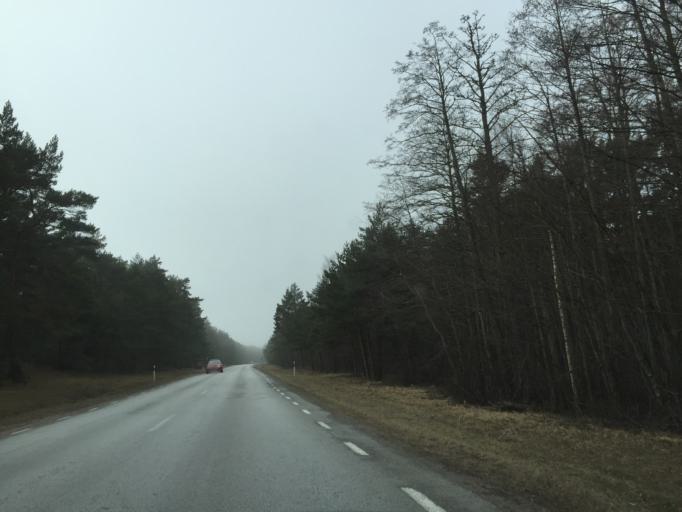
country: EE
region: Saare
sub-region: Kuressaare linn
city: Kuressaare
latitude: 58.1994
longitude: 22.2852
